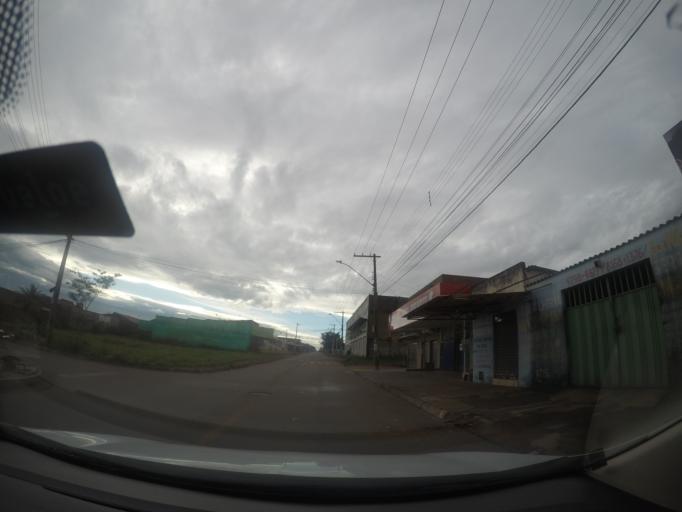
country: BR
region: Goias
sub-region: Goiania
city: Goiania
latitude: -16.6011
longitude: -49.3276
